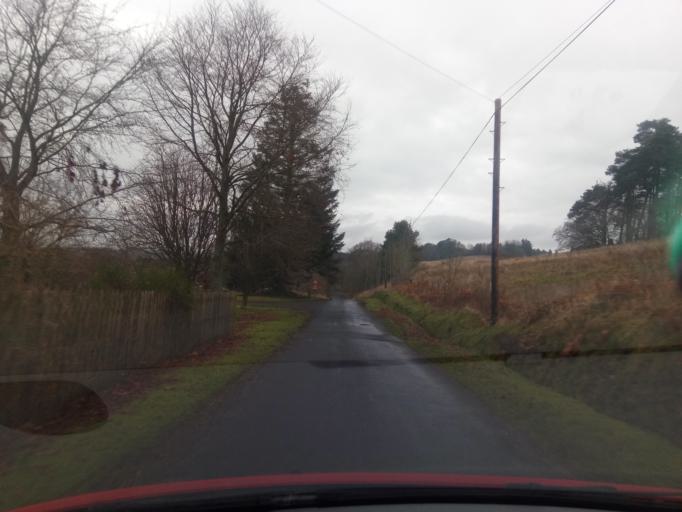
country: GB
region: England
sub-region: Northumberland
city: Rochester
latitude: 55.1796
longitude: -2.4320
